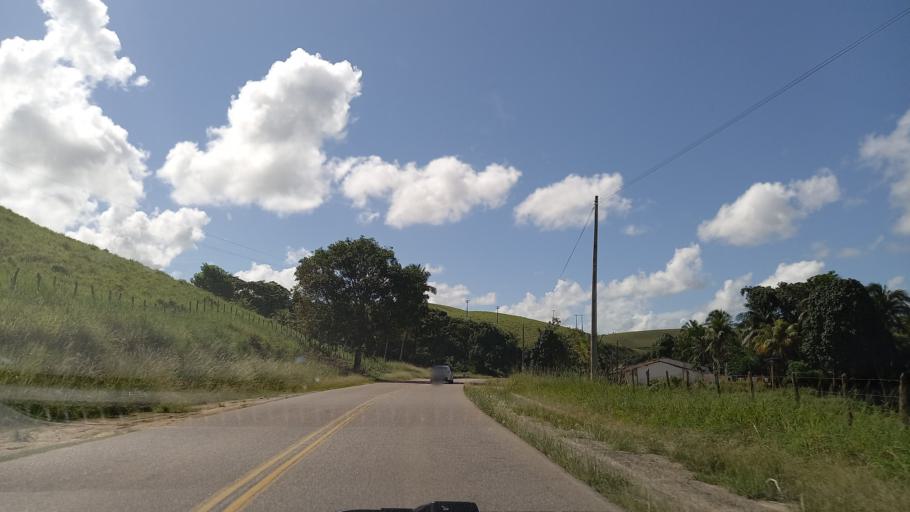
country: BR
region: Pernambuco
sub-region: Barreiros
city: Barreiros
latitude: -8.7526
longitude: -35.1717
